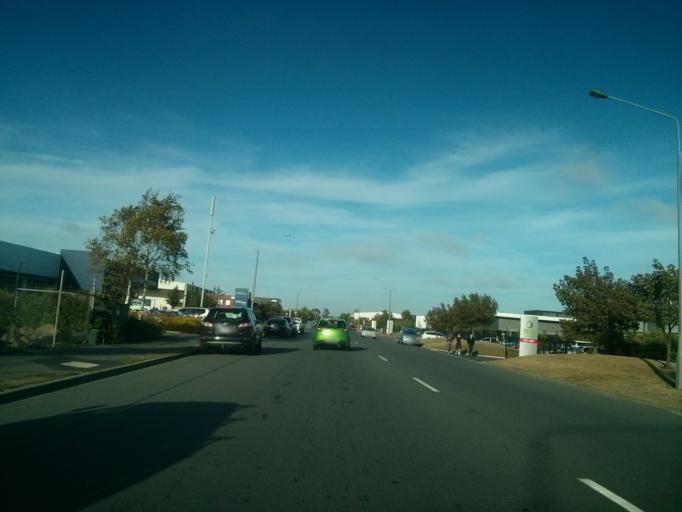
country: NZ
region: Canterbury
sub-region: Selwyn District
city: Prebbleton
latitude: -43.5376
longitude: 172.5403
